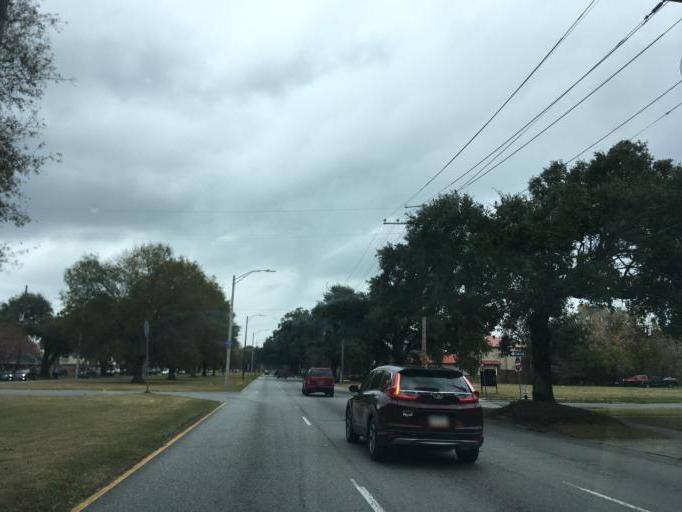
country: US
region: Louisiana
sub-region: Orleans Parish
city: New Orleans
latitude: 29.9936
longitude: -90.0587
